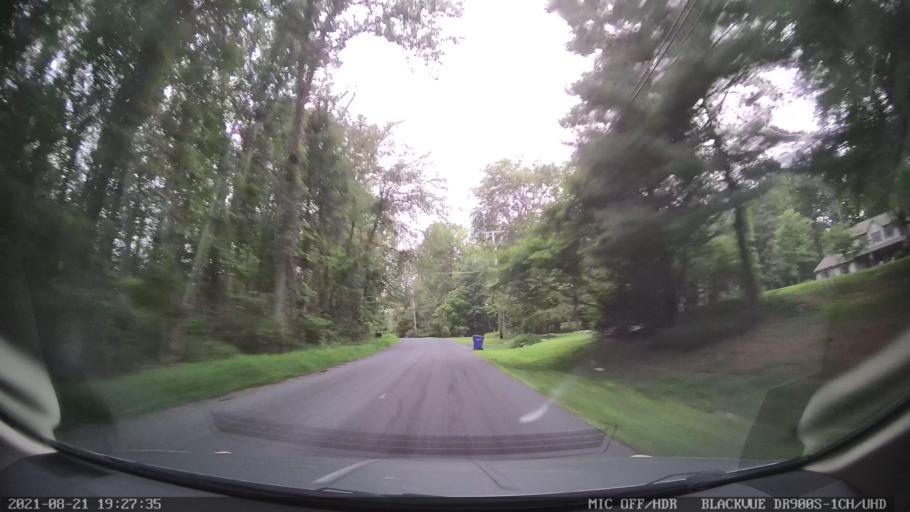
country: US
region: Pennsylvania
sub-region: Berks County
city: Oley
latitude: 40.4214
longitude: -75.7755
